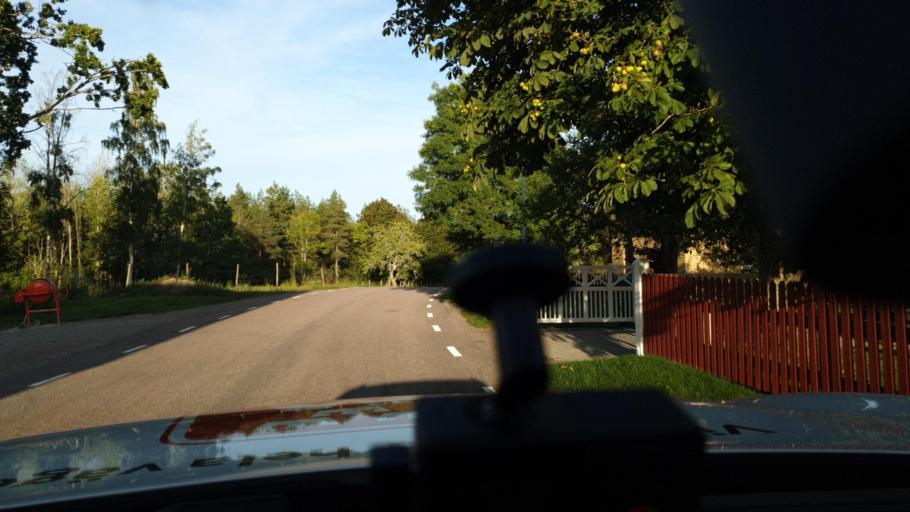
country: SE
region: Kalmar
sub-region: Hogsby Kommun
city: Hoegsby
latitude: 57.0217
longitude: 15.8575
